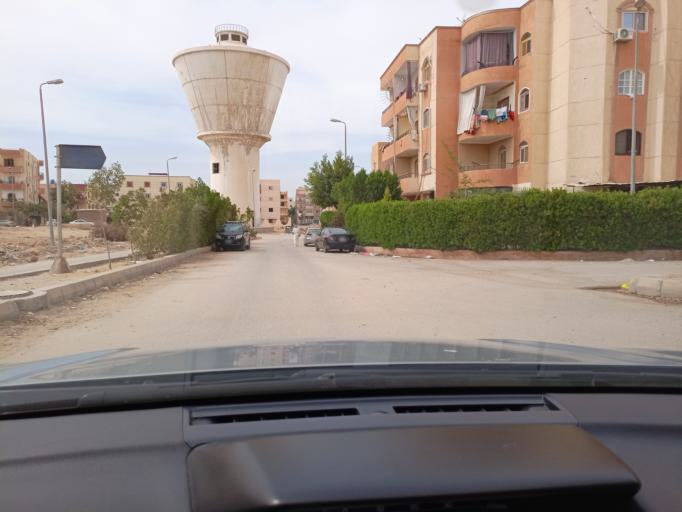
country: EG
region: Muhafazat al Qalyubiyah
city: Al Khankah
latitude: 30.2419
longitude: 31.4848
